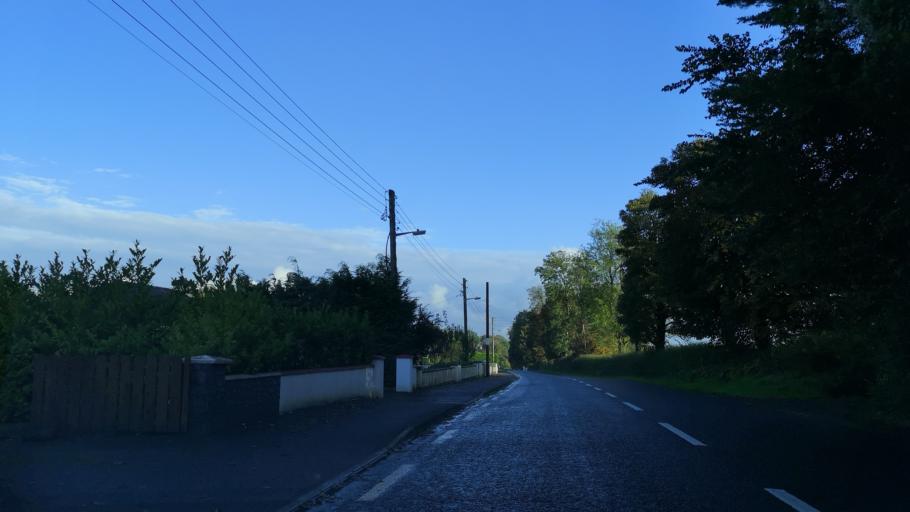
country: IE
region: Connaught
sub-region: Roscommon
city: Castlerea
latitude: 53.7627
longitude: -8.4755
